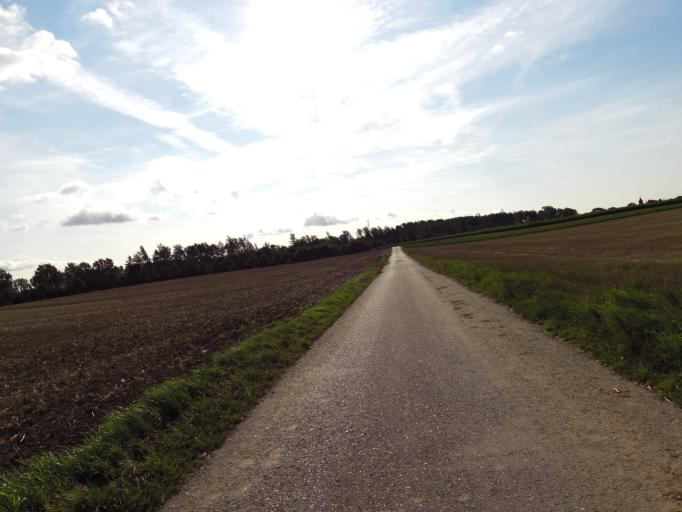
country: DE
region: North Rhine-Westphalia
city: Siersdorf
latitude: 50.9066
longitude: 6.2151
